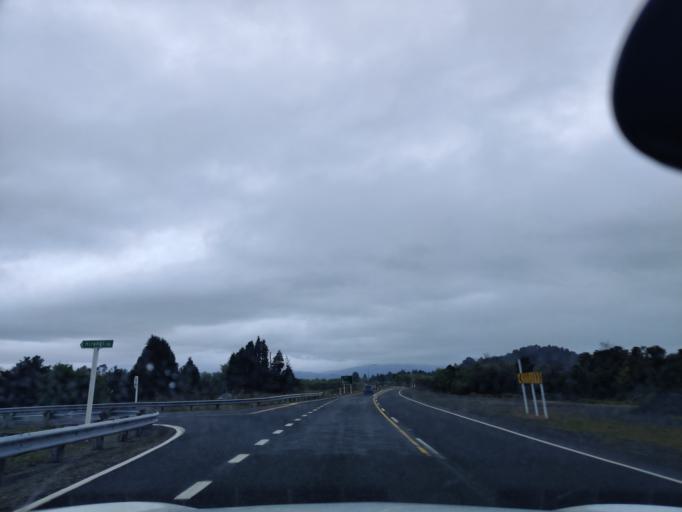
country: NZ
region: Waikato
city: Turangi
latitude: -38.9801
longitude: 175.7774
